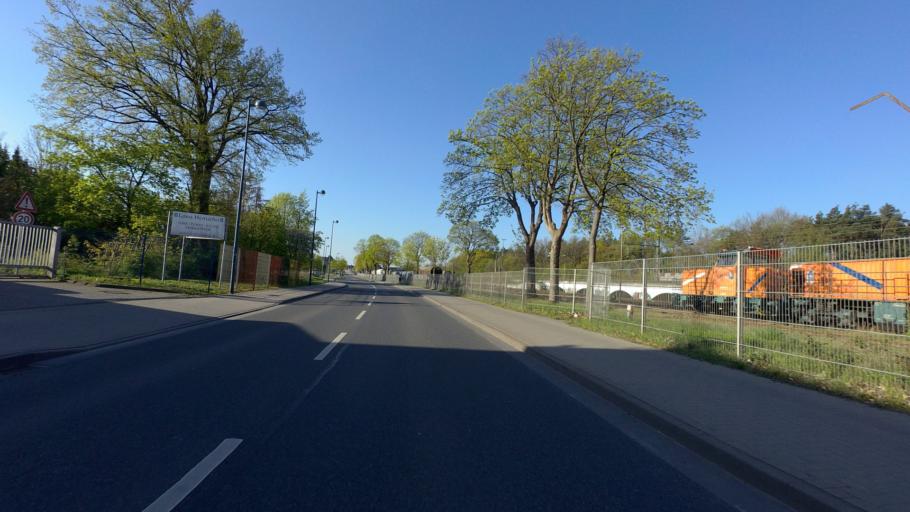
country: DE
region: Lower Saxony
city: Celle
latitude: 52.6272
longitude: 10.0650
